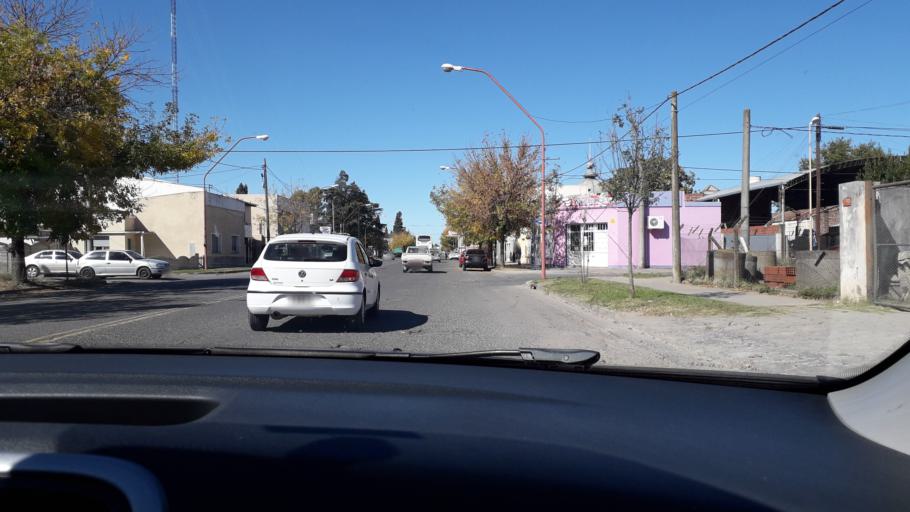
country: AR
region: Buenos Aires
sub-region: Partido de Azul
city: Azul
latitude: -36.7860
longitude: -59.8484
